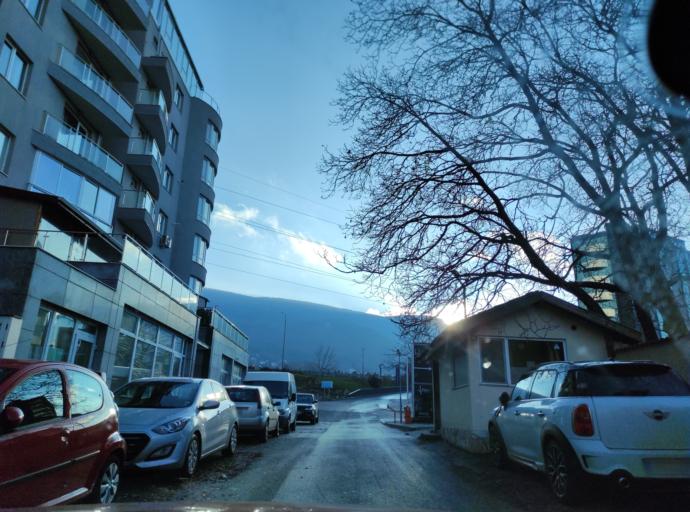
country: BG
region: Sofia-Capital
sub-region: Stolichna Obshtina
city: Sofia
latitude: 42.6560
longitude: 23.2820
